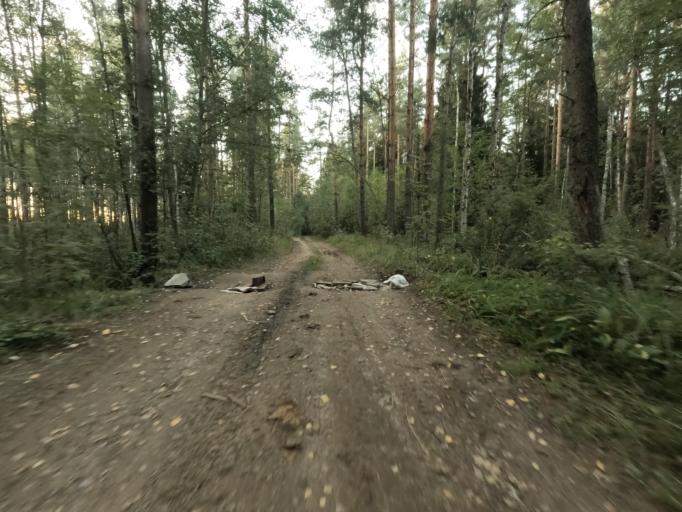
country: RU
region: Leningrad
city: Otradnoye
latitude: 59.8389
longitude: 30.8045
